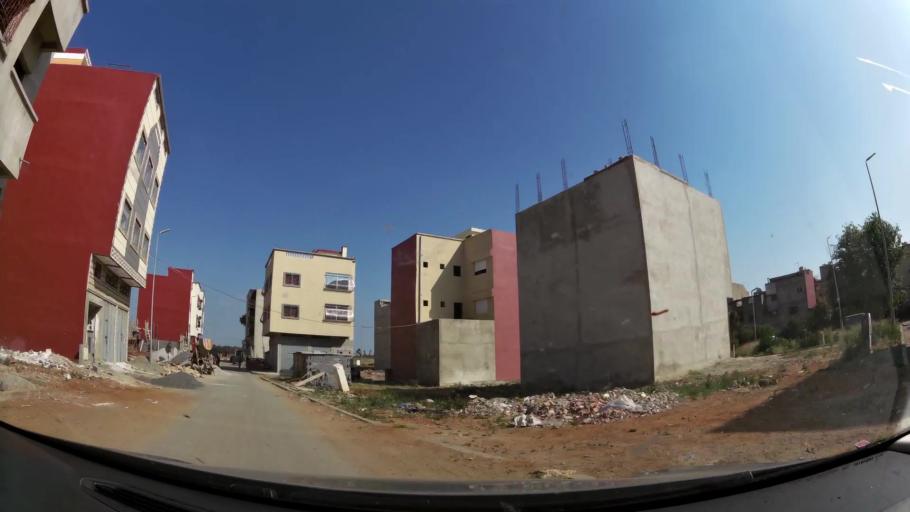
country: MA
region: Rabat-Sale-Zemmour-Zaer
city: Sale
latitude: 34.0618
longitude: -6.7676
